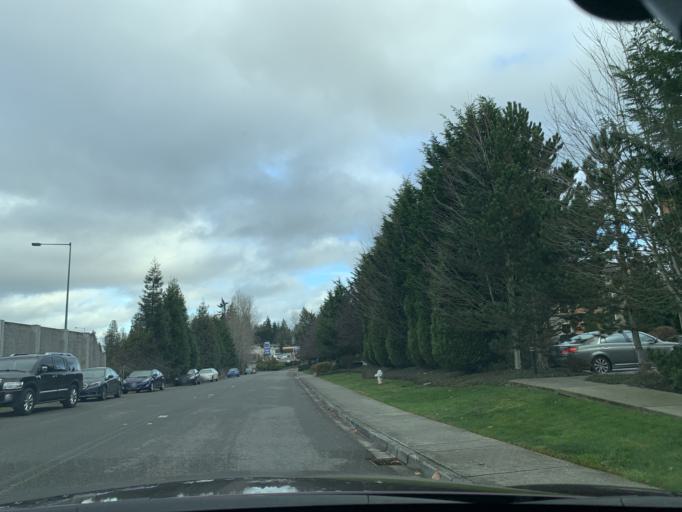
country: US
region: Washington
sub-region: King County
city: Kingsgate
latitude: 47.7417
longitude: -122.1862
